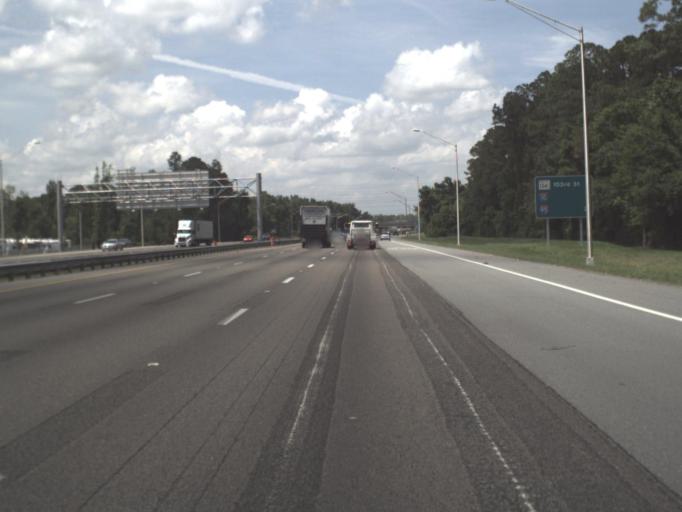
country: US
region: Florida
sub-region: Clay County
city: Bellair-Meadowbrook Terrace
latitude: 30.2194
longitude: -81.7616
